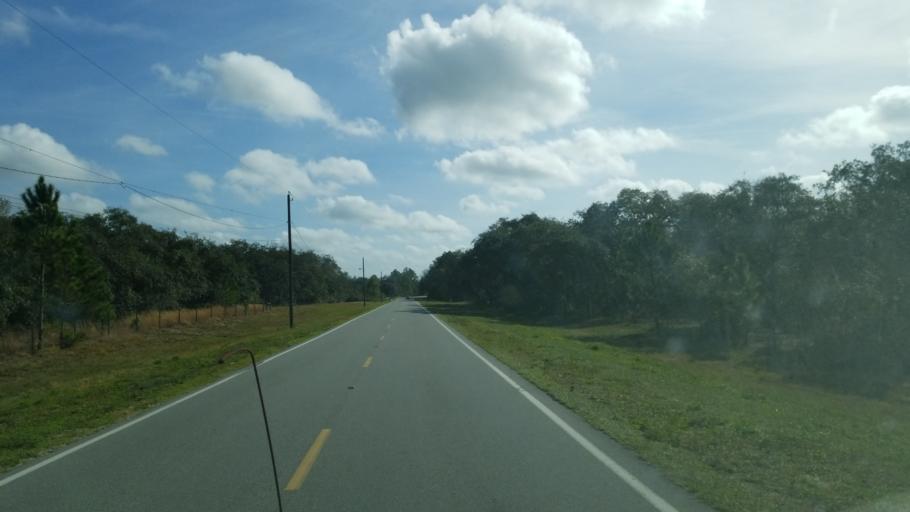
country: US
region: Florida
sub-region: Polk County
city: Polk City
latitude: 28.2585
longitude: -81.8146
